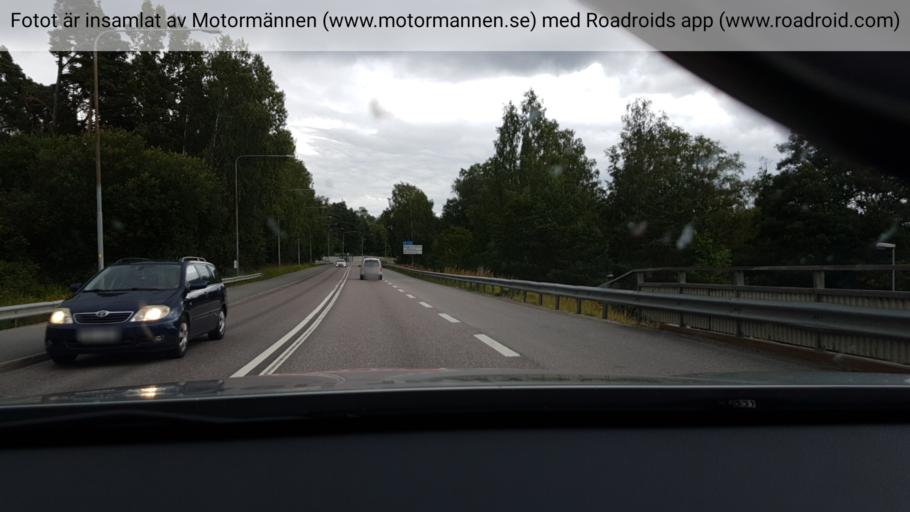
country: SE
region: Stockholm
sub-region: Tyreso Kommun
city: Bollmora
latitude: 59.2307
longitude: 18.1962
